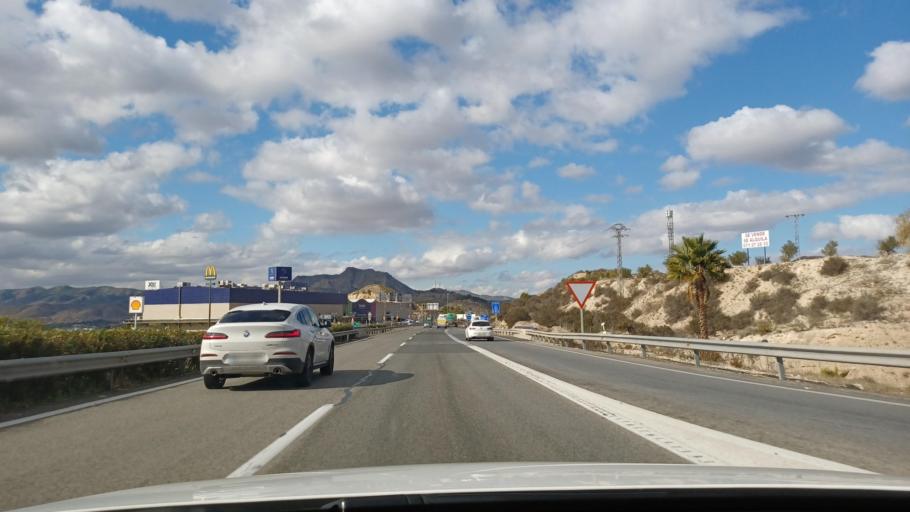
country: ES
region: Valencia
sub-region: Provincia de Alicante
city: Elda
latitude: 38.4894
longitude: -0.7744
